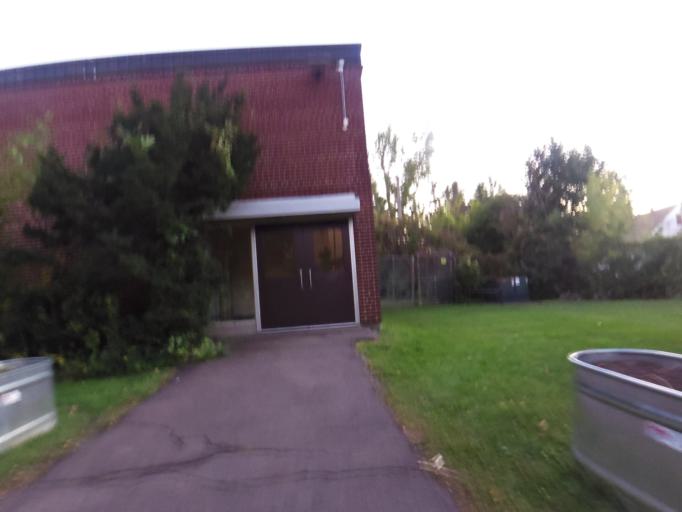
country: CA
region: Ontario
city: Ottawa
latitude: 45.3748
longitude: -75.6603
